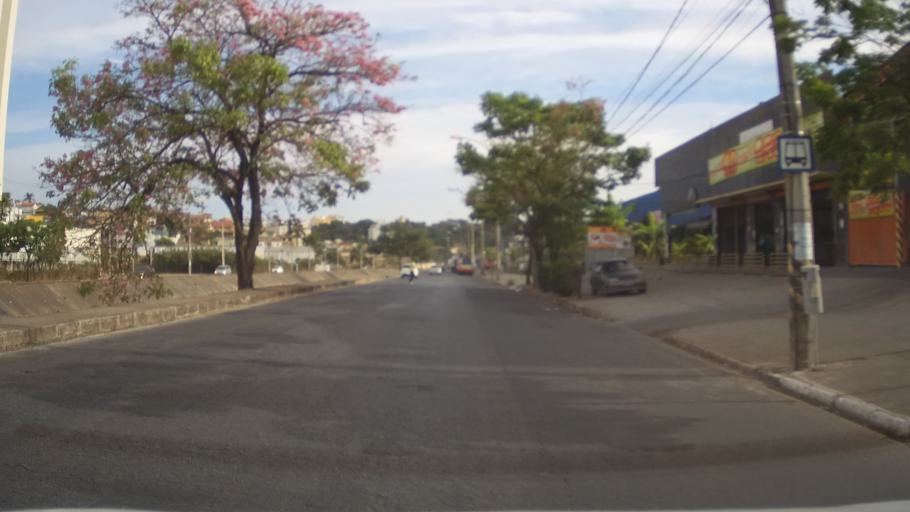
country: BR
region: Minas Gerais
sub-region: Contagem
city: Contagem
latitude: -19.8826
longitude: -44.0058
